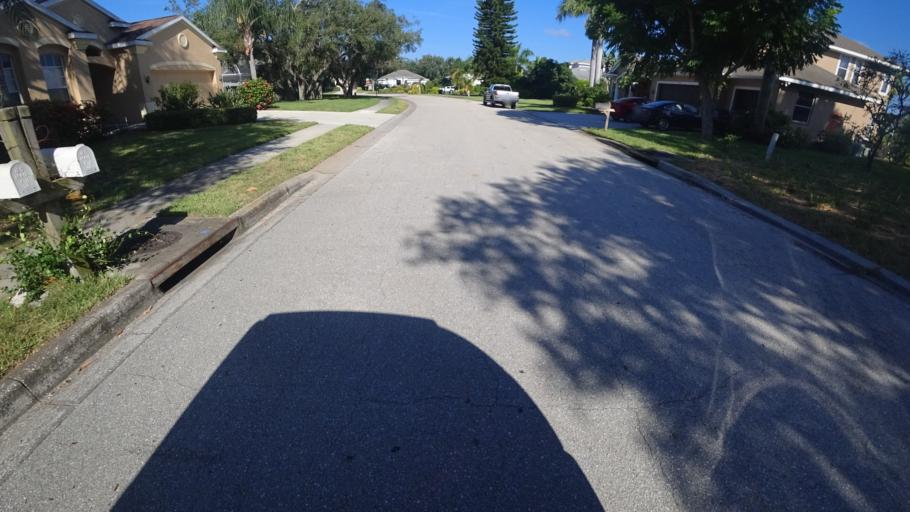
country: US
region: Florida
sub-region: Manatee County
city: Ellenton
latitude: 27.5051
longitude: -82.5171
